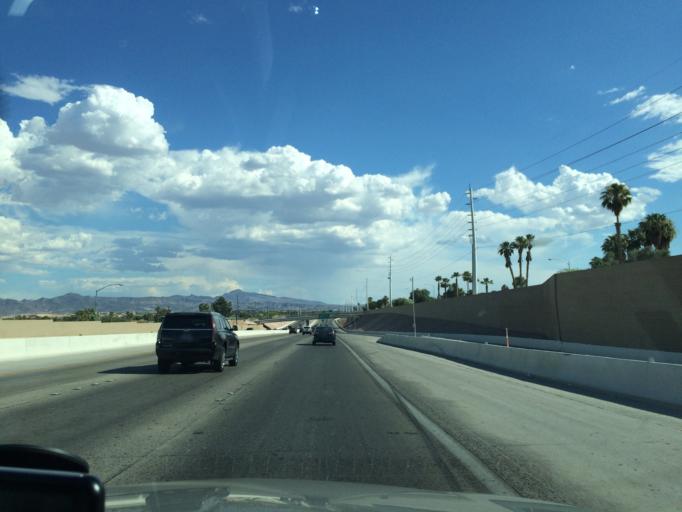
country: US
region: Nevada
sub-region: Clark County
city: Winchester
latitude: 36.1115
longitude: -115.0827
